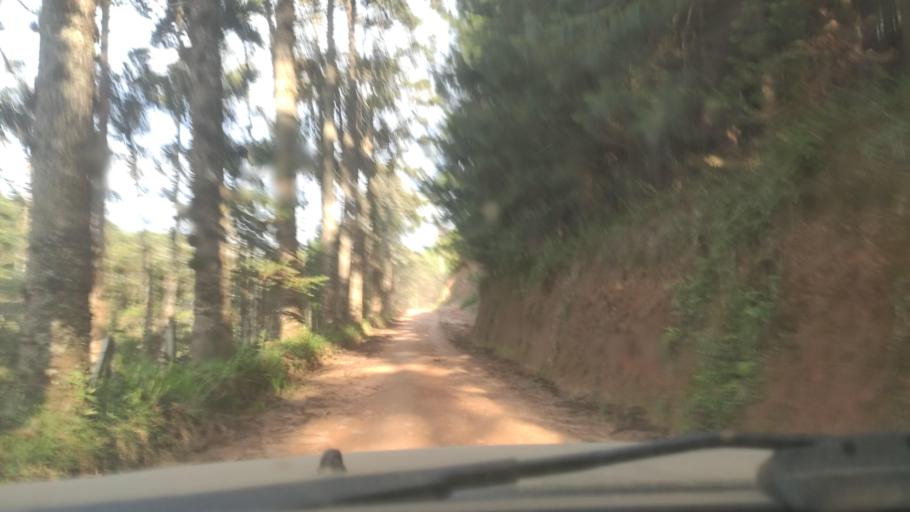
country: BR
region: Minas Gerais
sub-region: Cambui
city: Cambui
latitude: -22.7382
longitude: -45.9097
